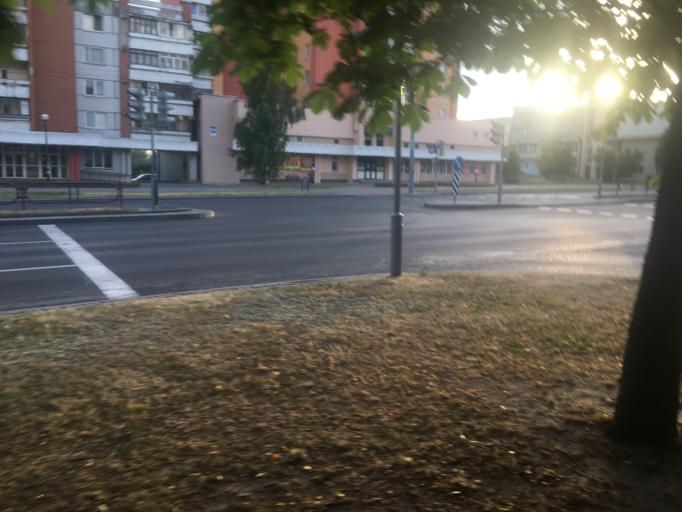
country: BY
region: Grodnenskaya
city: Hrodna
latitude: 53.6960
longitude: 23.8216
